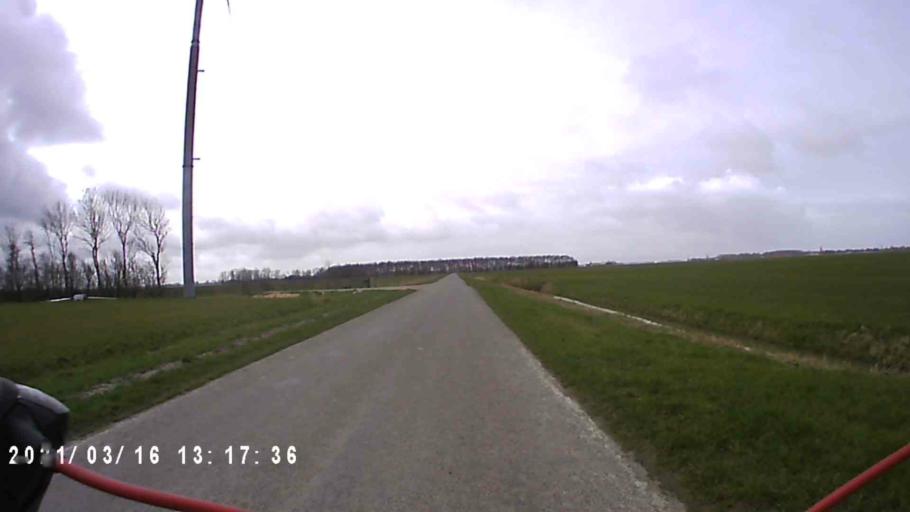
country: NL
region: Friesland
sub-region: Gemeente Het Bildt
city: Minnertsga
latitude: 53.2358
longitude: 5.5899
